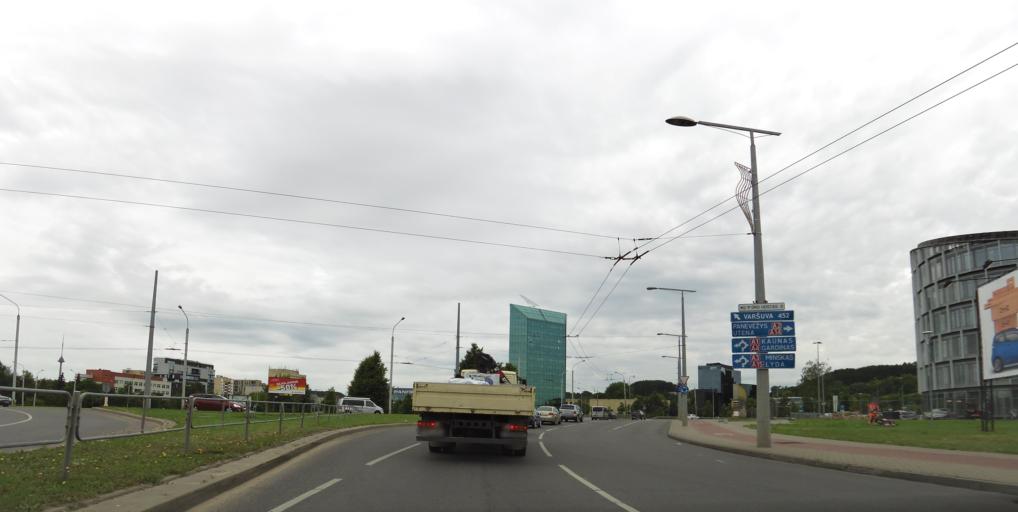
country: LT
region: Vilnius County
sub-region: Vilnius
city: Vilnius
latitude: 54.6985
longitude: 25.2656
